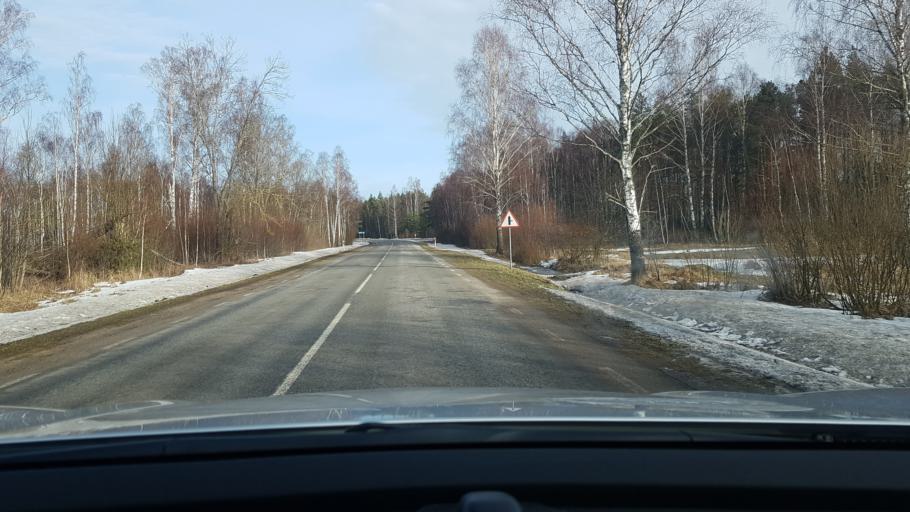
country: EE
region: Saare
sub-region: Kuressaare linn
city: Kuressaare
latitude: 58.4870
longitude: 22.7082
